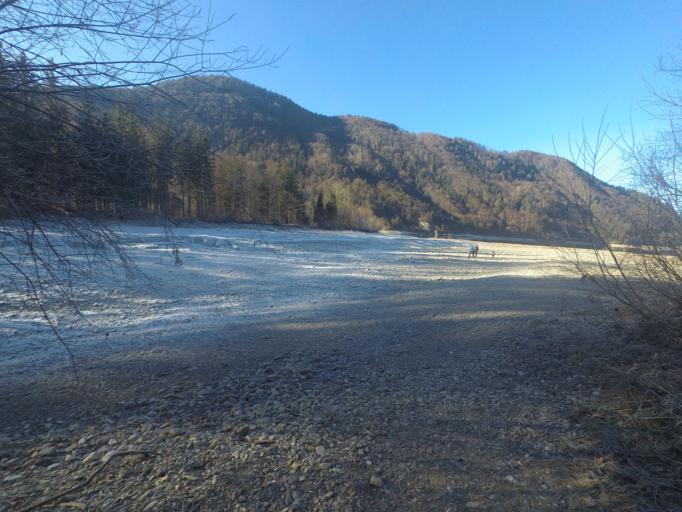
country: AT
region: Salzburg
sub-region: Politischer Bezirk Salzburg-Umgebung
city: Faistenau
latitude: 47.7474
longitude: 13.2523
